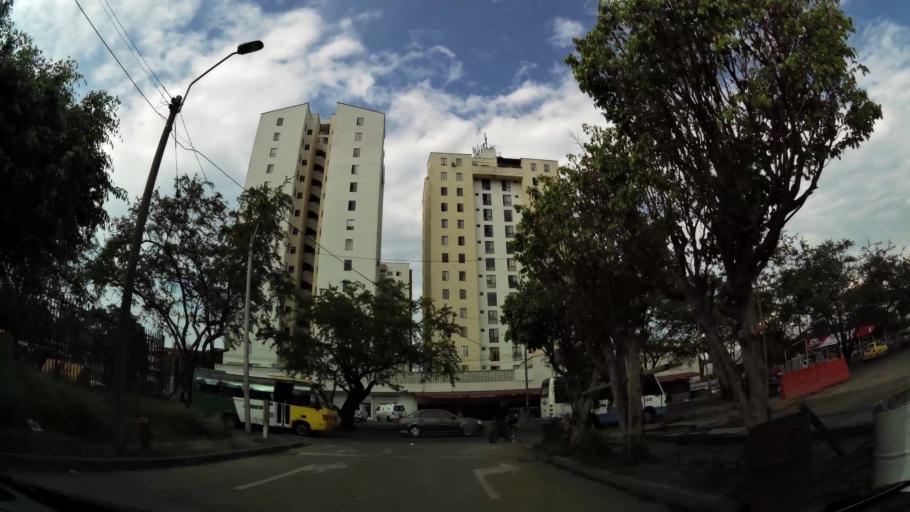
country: CO
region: Valle del Cauca
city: Cali
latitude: 3.4695
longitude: -76.5192
